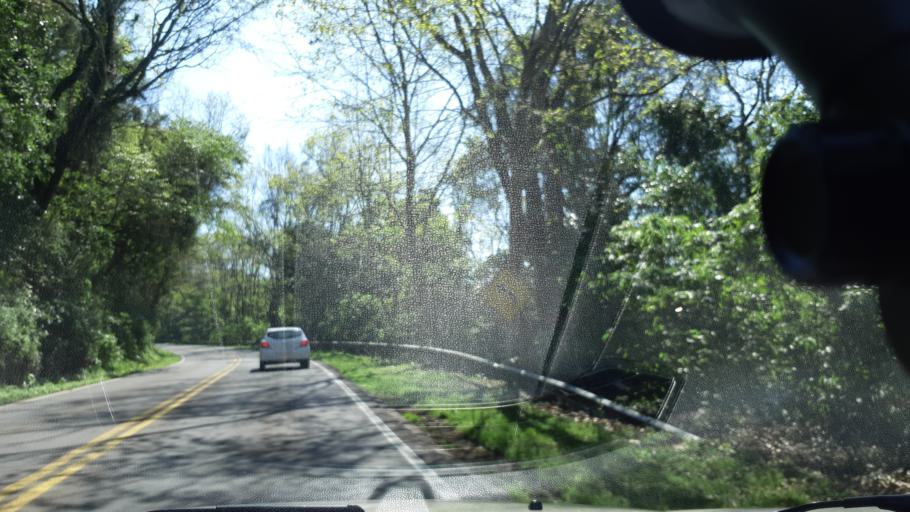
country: BR
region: Rio Grande do Sul
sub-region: Nova Petropolis
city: Nova Petropolis
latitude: -29.4006
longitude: -51.1269
